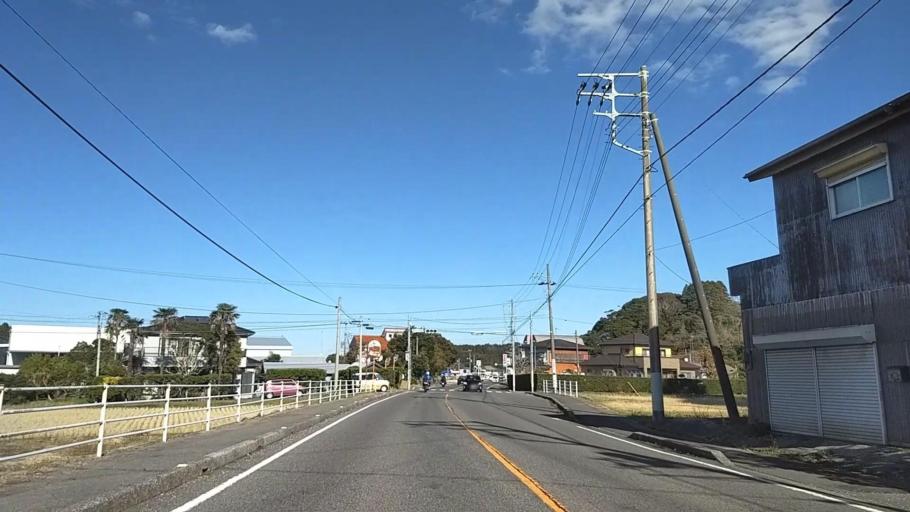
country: JP
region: Chiba
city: Ohara
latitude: 35.2188
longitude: 140.3791
